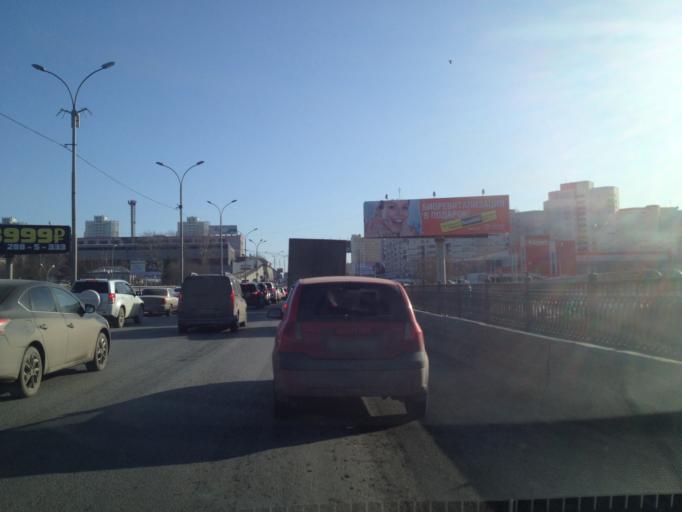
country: RU
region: Sverdlovsk
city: Yekaterinburg
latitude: 56.8413
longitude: 60.5624
